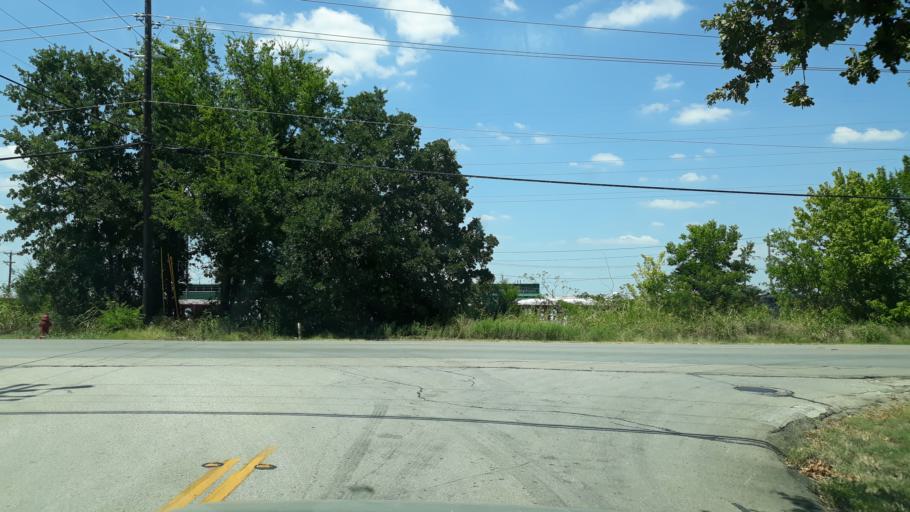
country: US
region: Texas
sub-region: Tarrant County
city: Euless
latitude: 32.8160
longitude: -97.0202
